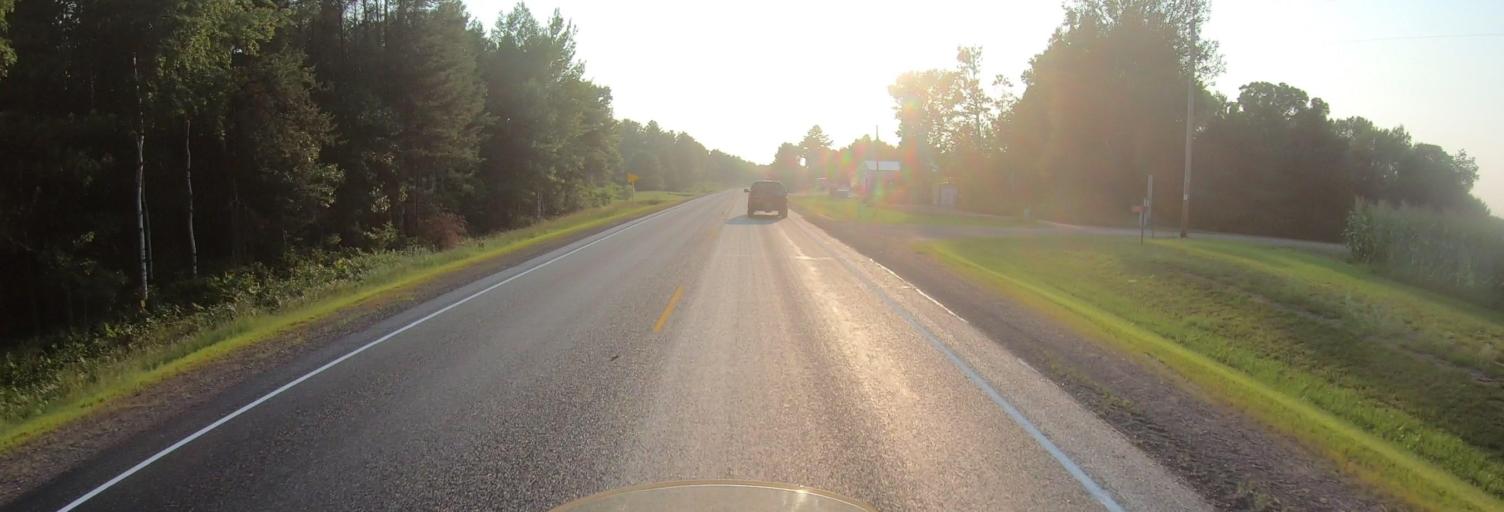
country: US
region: Wisconsin
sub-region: Washburn County
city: Spooner
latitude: 45.8216
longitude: -91.9199
